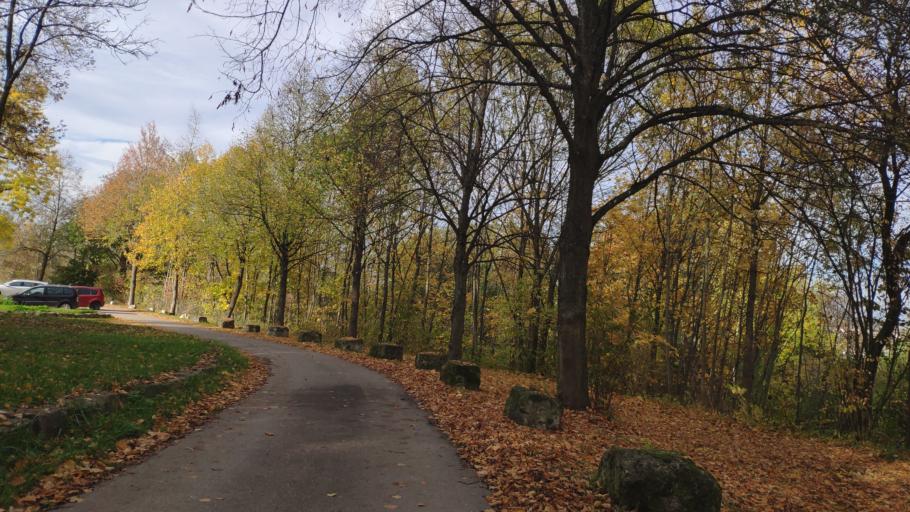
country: DE
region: Baden-Wuerttemberg
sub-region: Tuebingen Region
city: Ulm
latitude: 48.3830
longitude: 9.9516
